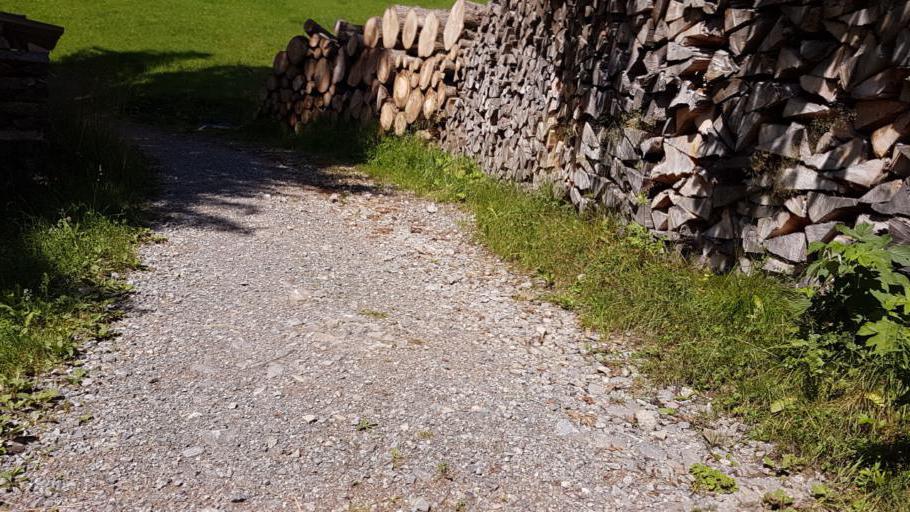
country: CH
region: Bern
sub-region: Frutigen-Niedersimmental District
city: Adelboden
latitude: 46.5140
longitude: 7.6033
